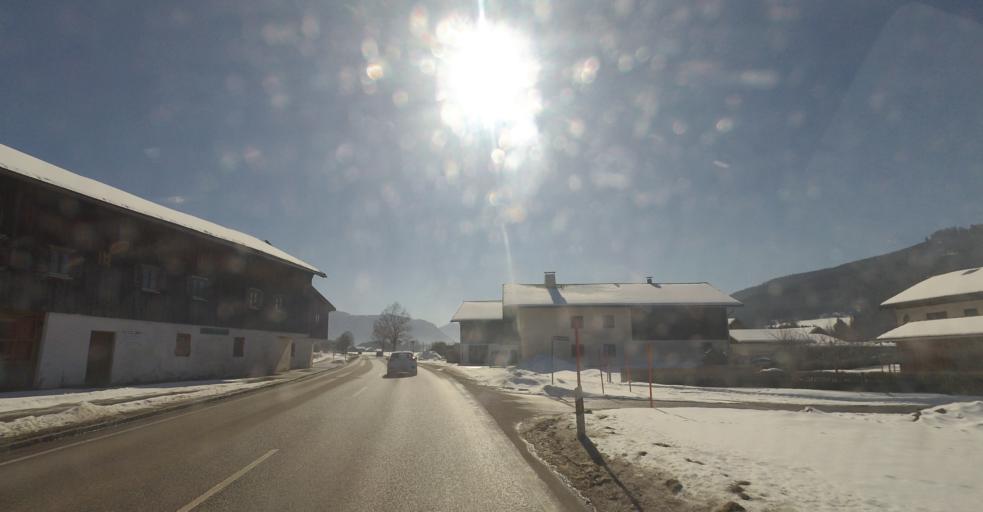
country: DE
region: Bavaria
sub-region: Upper Bavaria
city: Inzell
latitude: 47.7954
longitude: 12.7197
